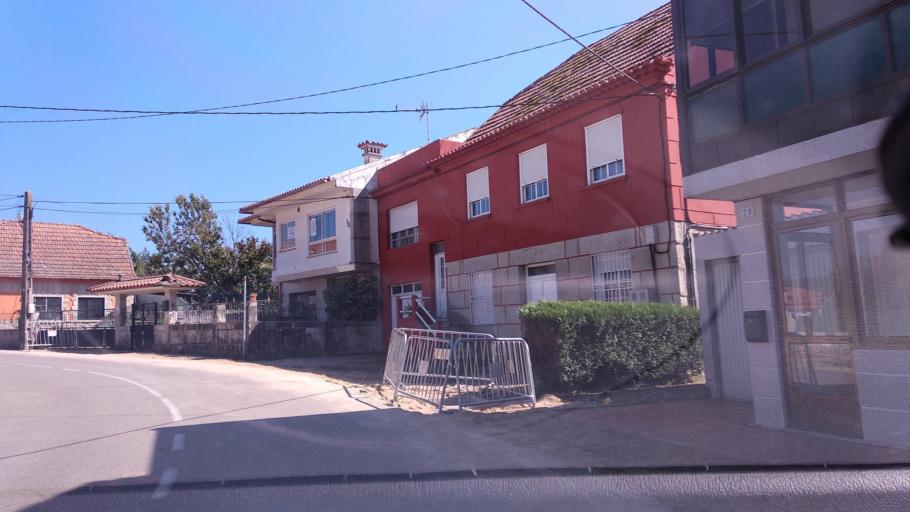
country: ES
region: Galicia
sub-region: Provincia de Pontevedra
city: Moana
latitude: 42.2808
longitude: -8.7495
